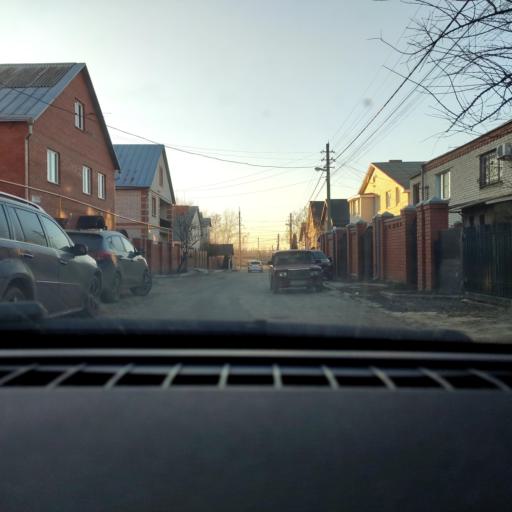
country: RU
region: Voronezj
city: Maslovka
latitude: 51.6274
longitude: 39.2815
